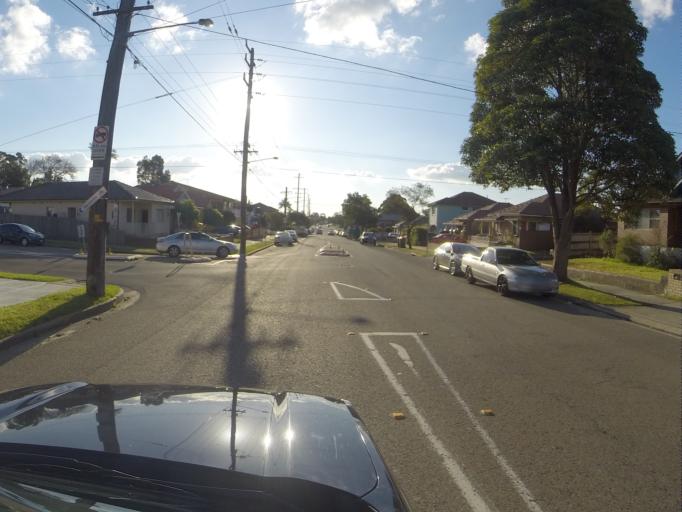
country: AU
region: New South Wales
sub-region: Rockdale
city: Bexley
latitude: -33.9512
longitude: 151.1162
